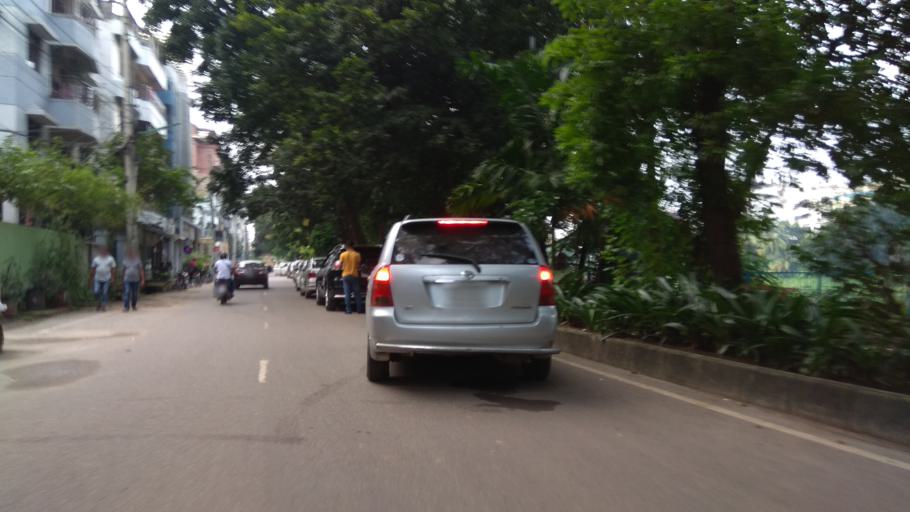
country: BD
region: Dhaka
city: Tungi
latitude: 23.8674
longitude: 90.3922
